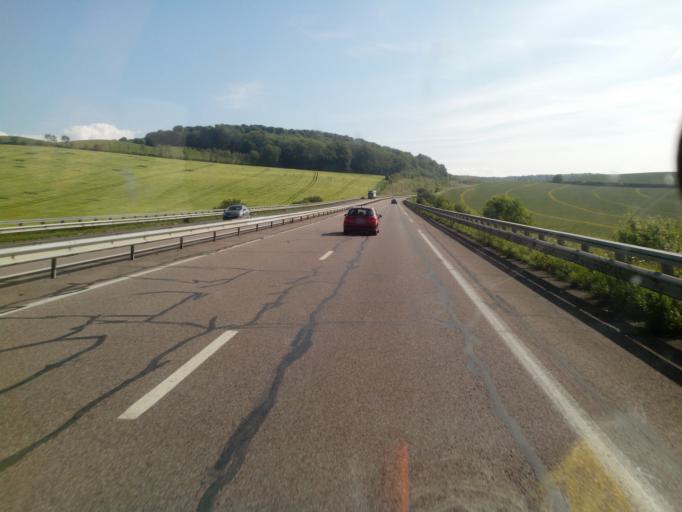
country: FR
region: Haute-Normandie
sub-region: Departement de la Seine-Maritime
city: Blangy-sur-Bresle
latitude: 49.9183
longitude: 1.6339
